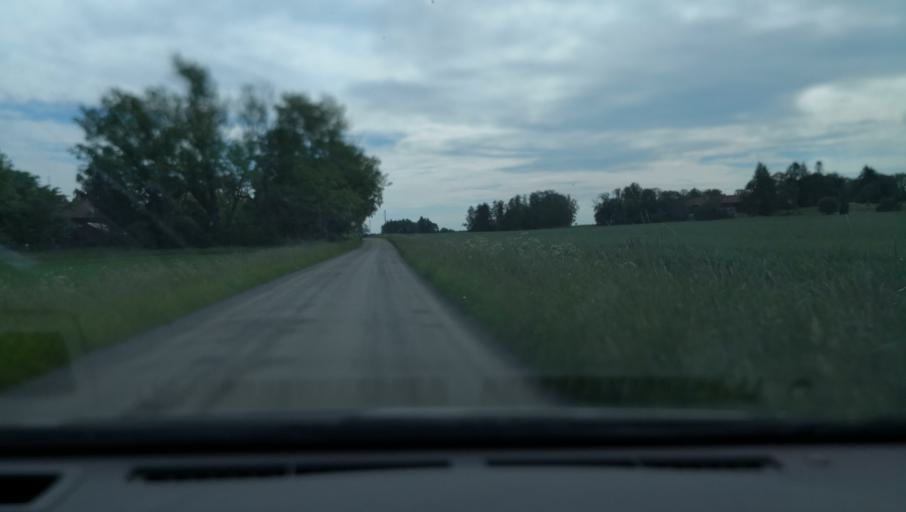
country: SE
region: Uppsala
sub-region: Enkopings Kommun
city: Enkoping
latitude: 59.7041
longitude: 17.1540
